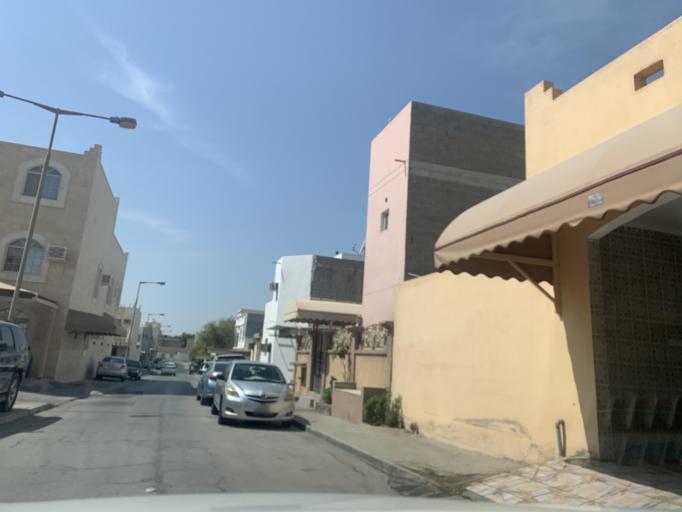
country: BH
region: Central Governorate
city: Madinat Hamad
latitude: 26.1380
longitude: 50.5064
